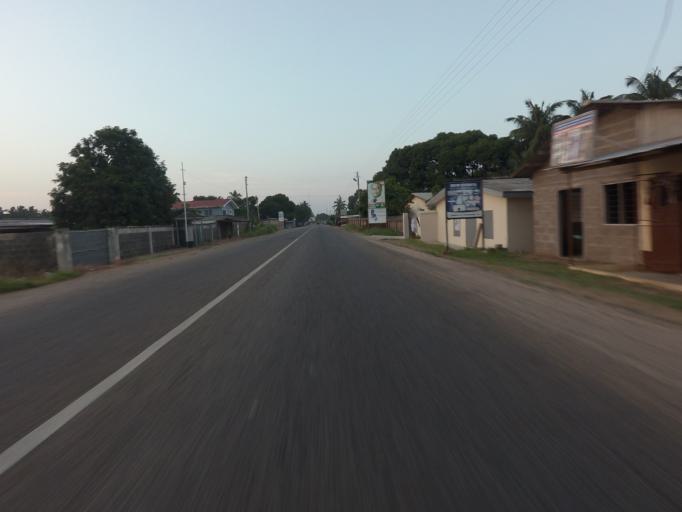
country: GH
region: Volta
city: Keta
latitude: 5.8736
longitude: 0.9801
